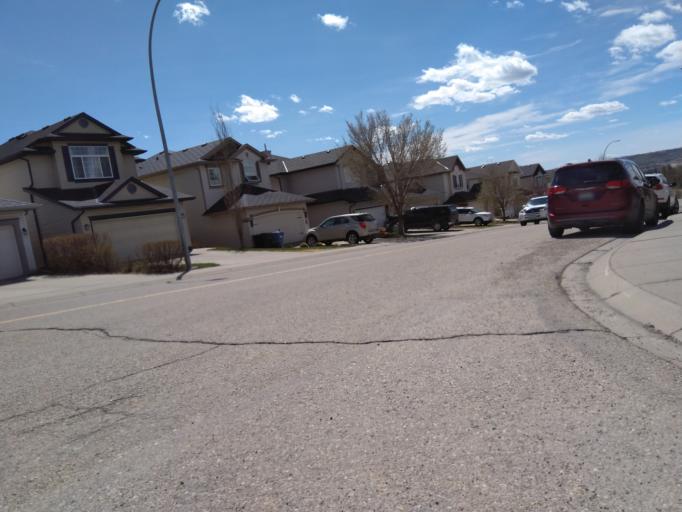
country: CA
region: Alberta
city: Calgary
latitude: 51.1318
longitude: -114.2420
